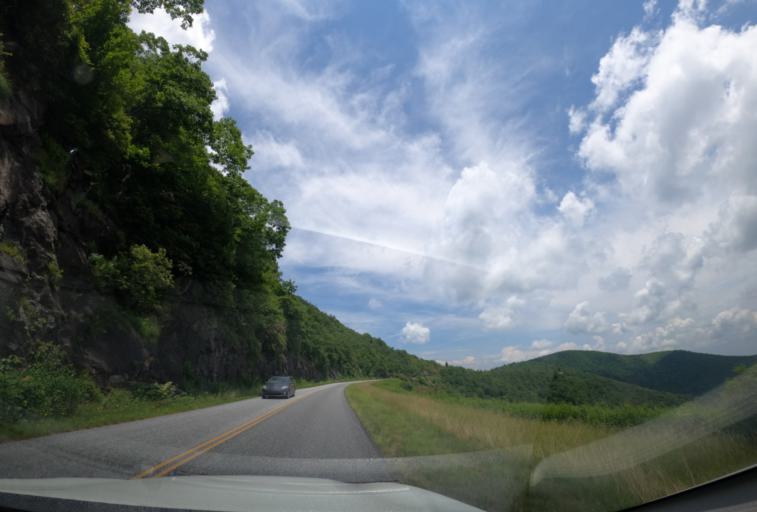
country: US
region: North Carolina
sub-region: Haywood County
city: Canton
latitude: 35.3992
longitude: -82.7602
